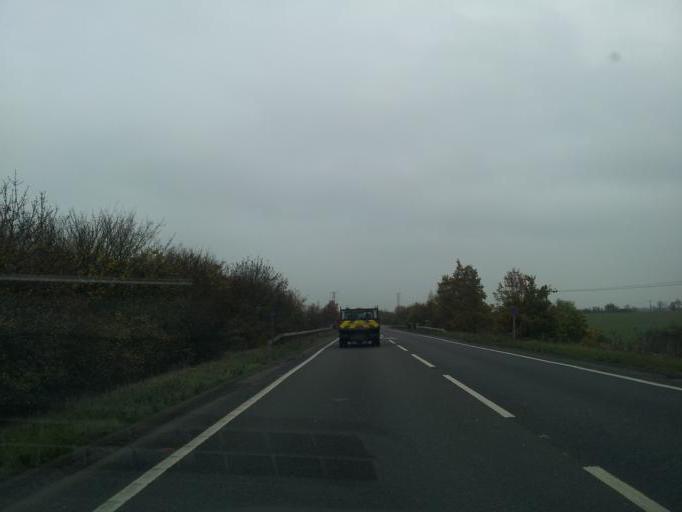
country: GB
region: England
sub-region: Cambridgeshire
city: Saint Neots
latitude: 52.2139
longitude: -0.2483
